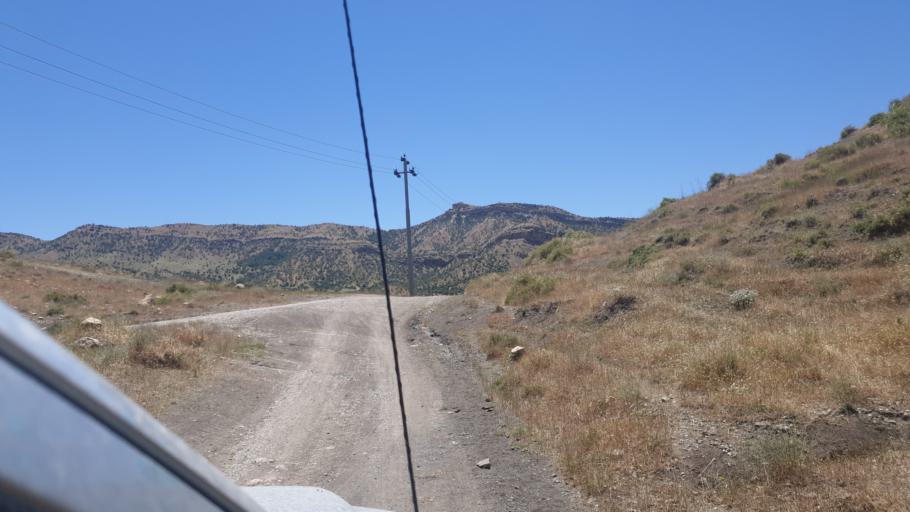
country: IQ
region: Arbil
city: Nahiyat Hiran
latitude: 36.2003
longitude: 44.4227
